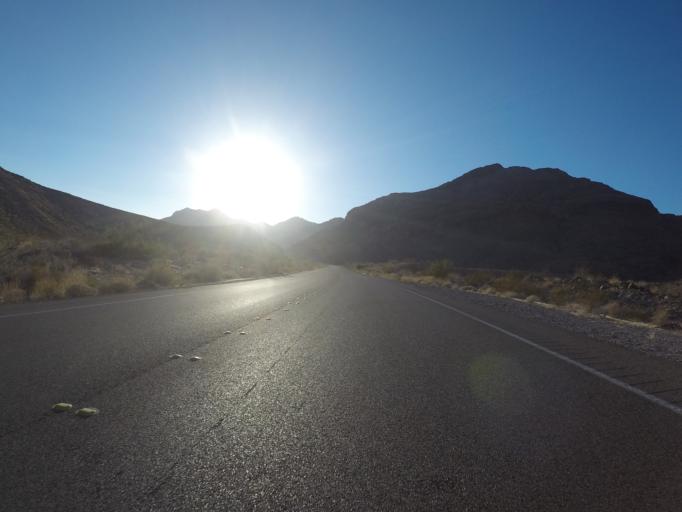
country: US
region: Nevada
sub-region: Clark County
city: Moapa Valley
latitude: 36.3626
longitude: -114.4778
